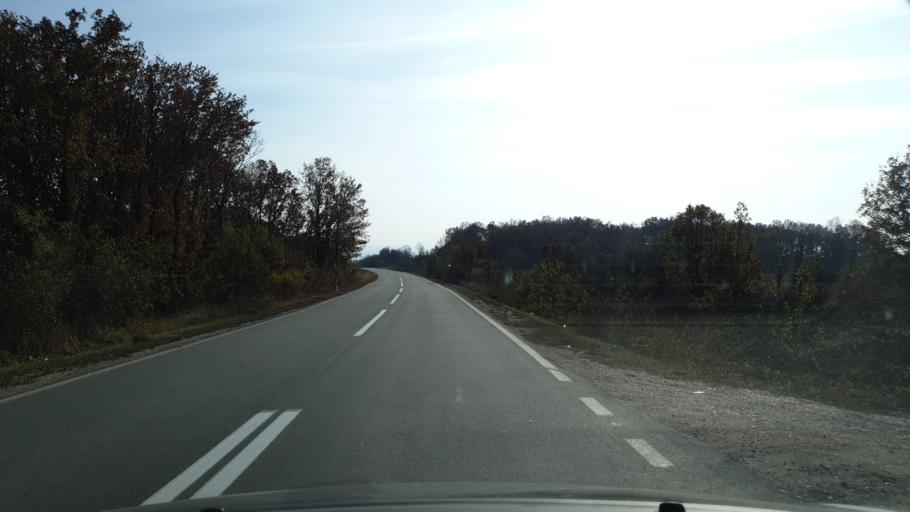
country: RS
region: Central Serbia
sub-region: Borski Okrug
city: Bor
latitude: 43.9847
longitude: 22.0719
